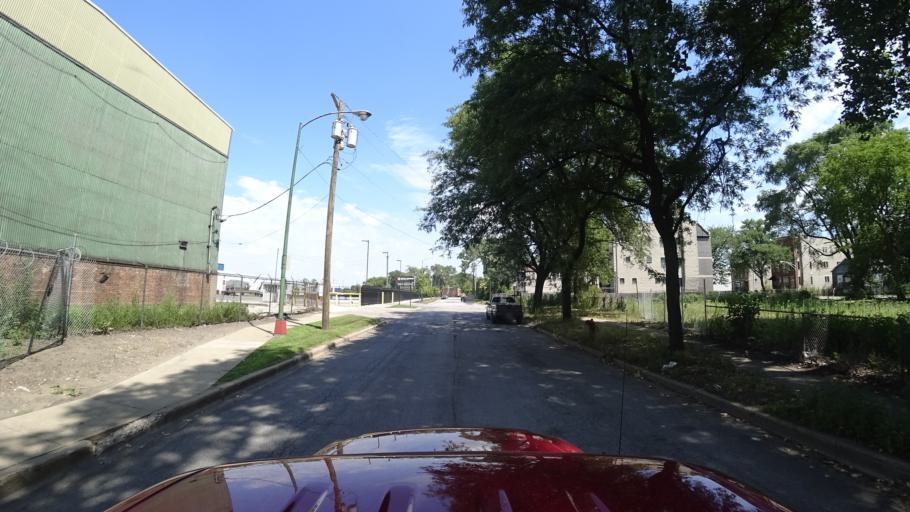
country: US
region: Illinois
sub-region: Cook County
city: Chicago
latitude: 41.8219
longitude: -87.6332
